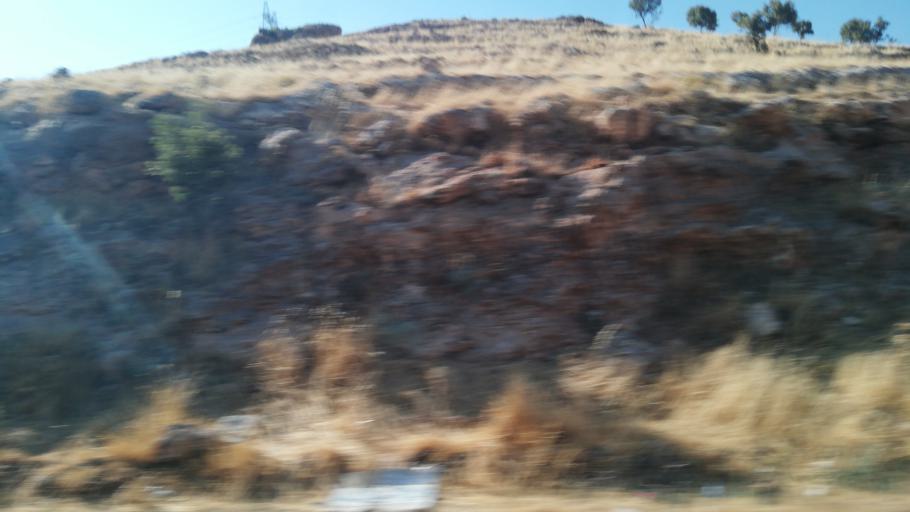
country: TR
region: Mardin
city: Sivrice
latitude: 37.2359
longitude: 41.3412
